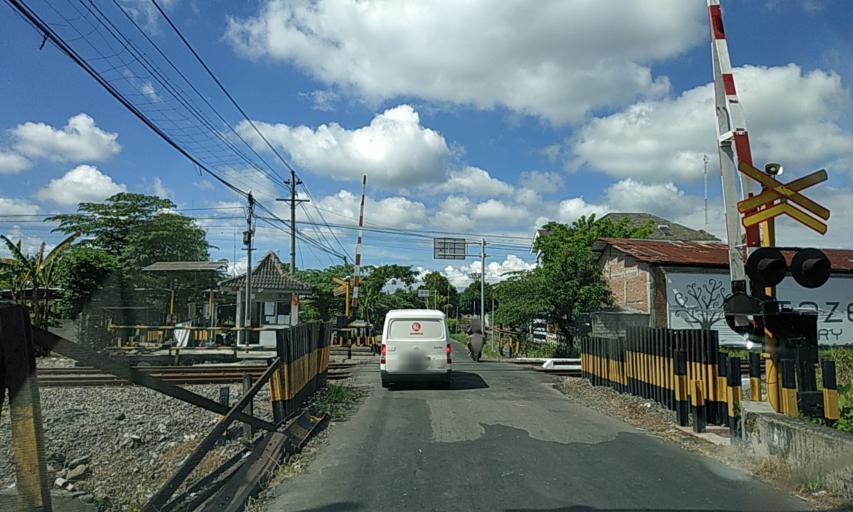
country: ID
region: Central Java
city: Trucuk
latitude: -7.6894
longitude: 110.6443
